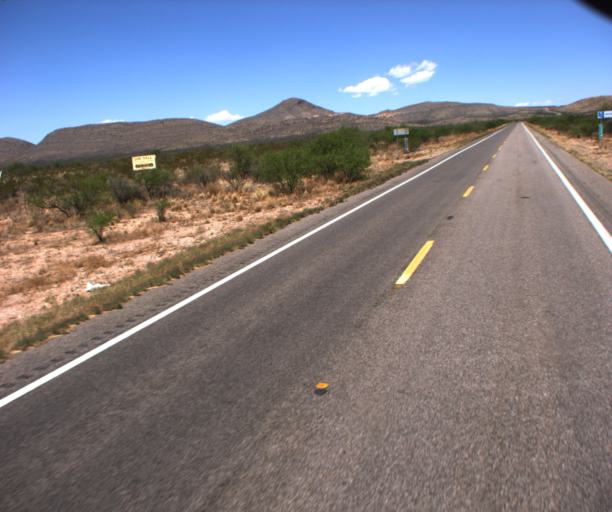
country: US
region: Arizona
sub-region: Cochise County
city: Tombstone
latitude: 31.6326
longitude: -110.0457
